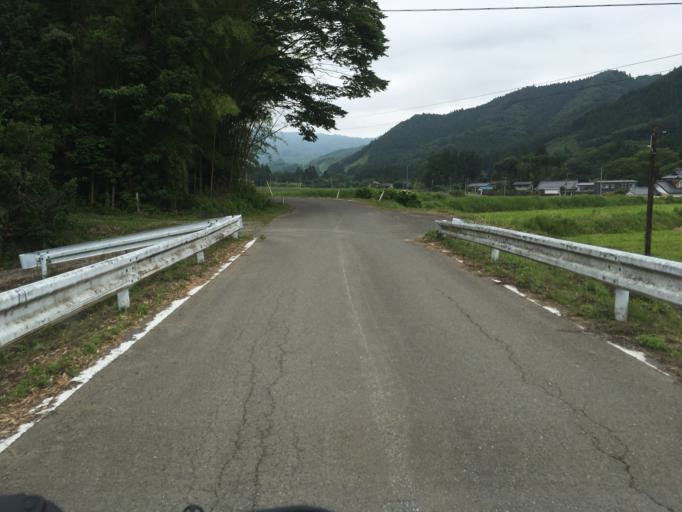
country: JP
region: Miyagi
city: Marumori
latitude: 37.7677
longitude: 140.8435
